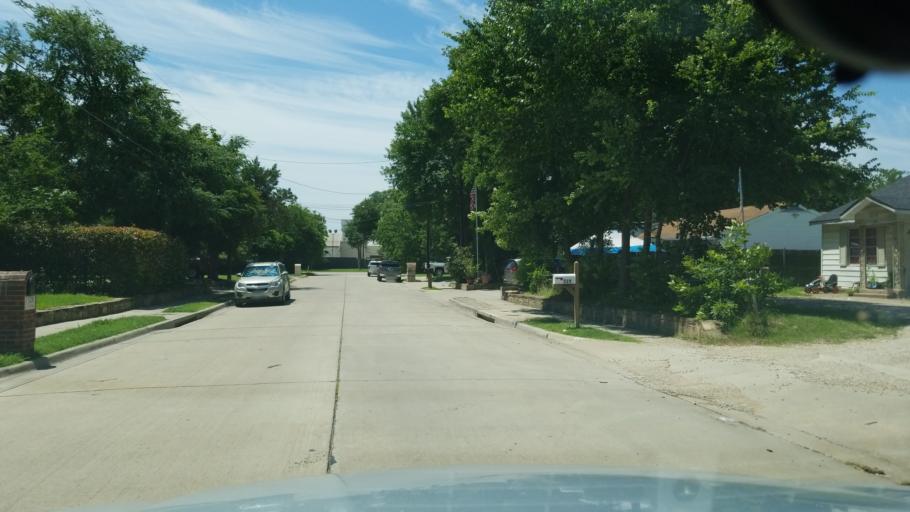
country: US
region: Texas
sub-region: Dallas County
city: Irving
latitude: 32.8188
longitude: -96.9360
